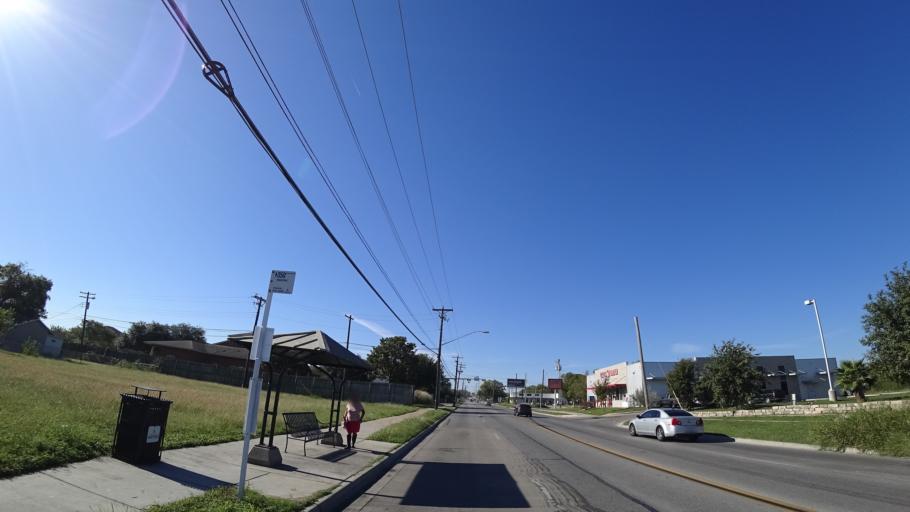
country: US
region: Texas
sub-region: Travis County
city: Austin
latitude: 30.2287
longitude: -97.7010
